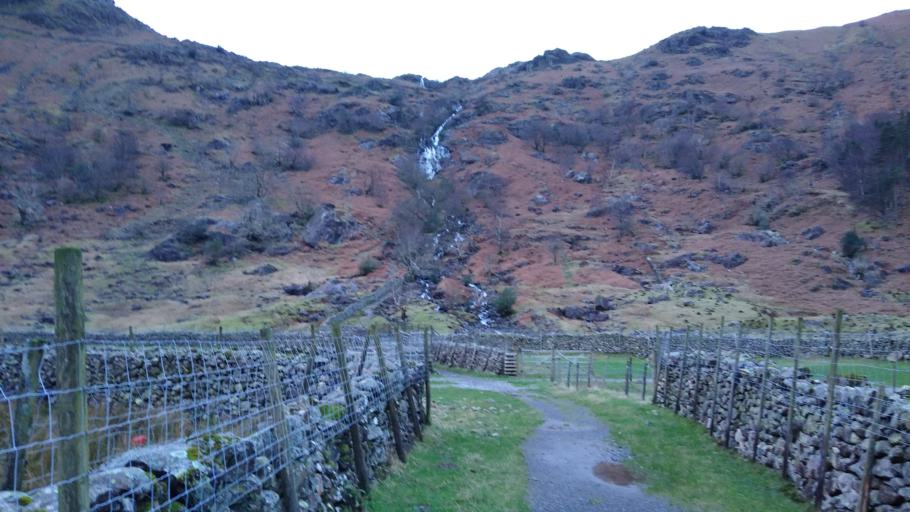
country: GB
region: England
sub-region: Cumbria
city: Keswick
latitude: 54.4993
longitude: -3.1837
